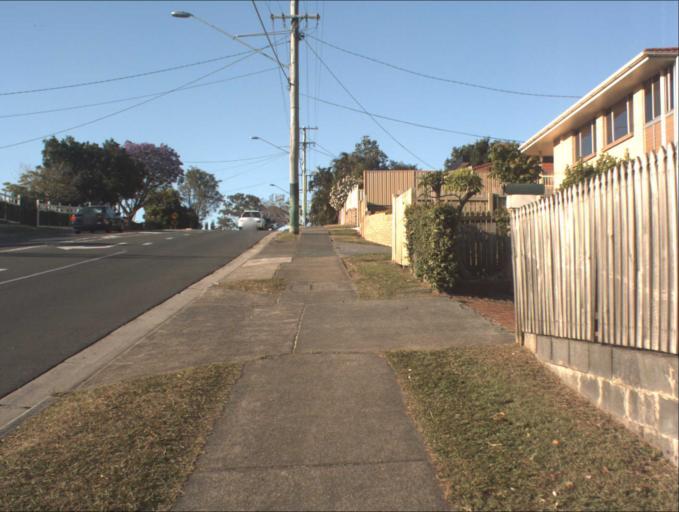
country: AU
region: Queensland
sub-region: Logan
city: Rochedale South
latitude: -27.5999
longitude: 153.1213
